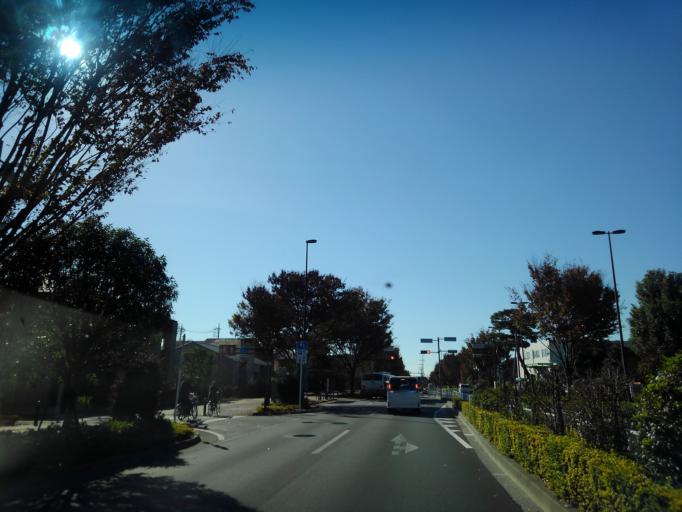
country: JP
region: Tokyo
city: Mitaka-shi
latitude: 35.6758
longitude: 139.5461
